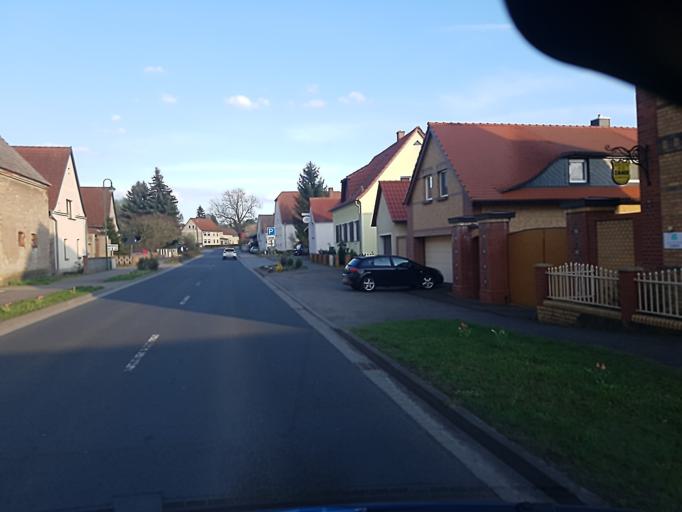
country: DE
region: Saxony
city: Bad Duben
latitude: 51.6249
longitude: 12.5577
